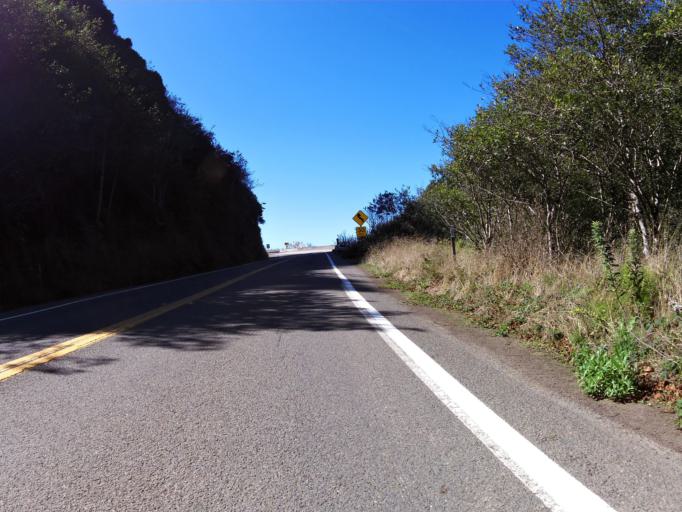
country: US
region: California
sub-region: Mendocino County
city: Fort Bragg
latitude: 39.7109
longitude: -123.8050
